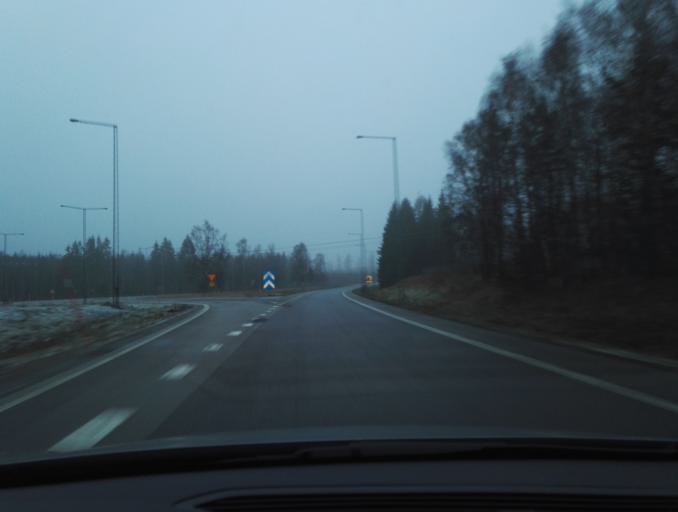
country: SE
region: Kronoberg
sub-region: Vaxjo Kommun
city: Vaexjoe
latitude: 56.8975
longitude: 14.7312
